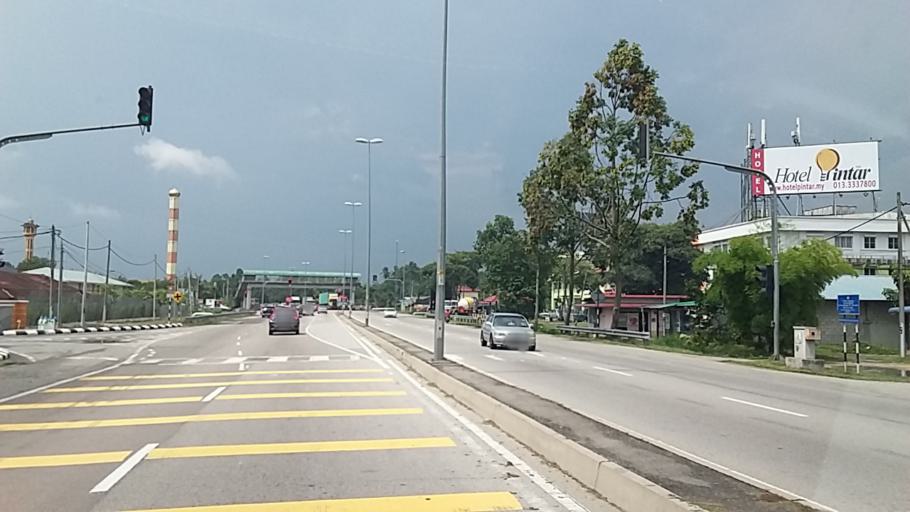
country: MY
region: Johor
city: Parit Raja
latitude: 1.8567
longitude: 103.0979
